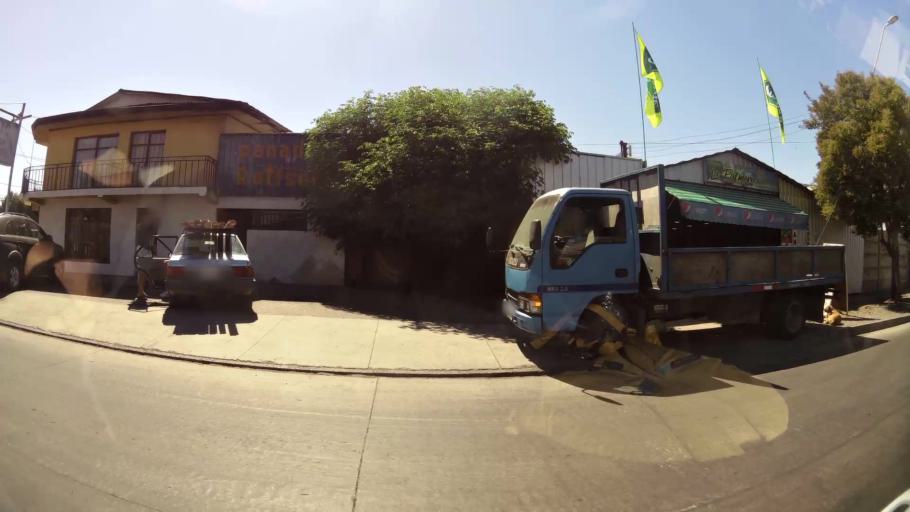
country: CL
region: Maule
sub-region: Provincia de Curico
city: Curico
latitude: -34.9695
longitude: -71.2481
